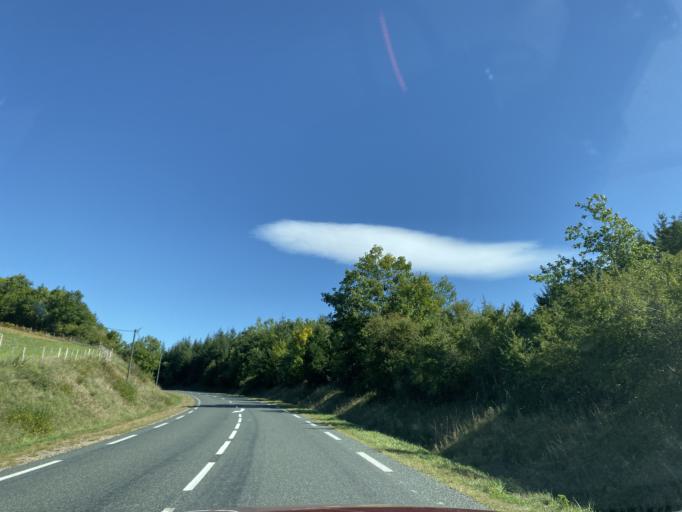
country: FR
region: Rhone-Alpes
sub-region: Departement de la Loire
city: Saint-Just-en-Chevalet
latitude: 45.8944
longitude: 3.8461
